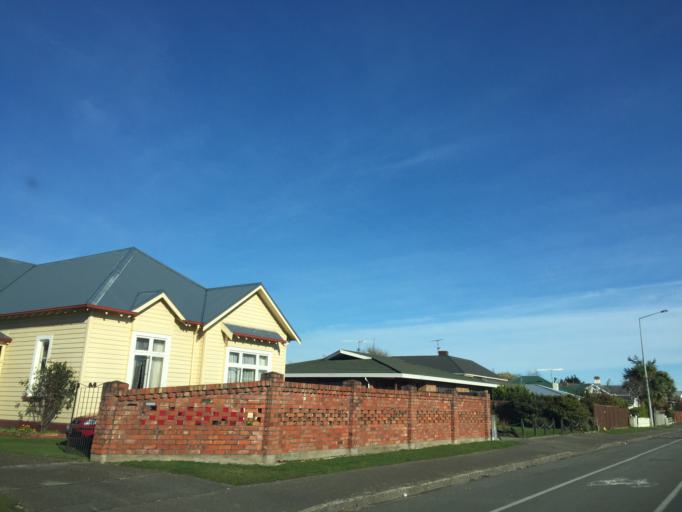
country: NZ
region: Southland
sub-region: Invercargill City
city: Invercargill
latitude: -46.4077
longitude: 168.3681
